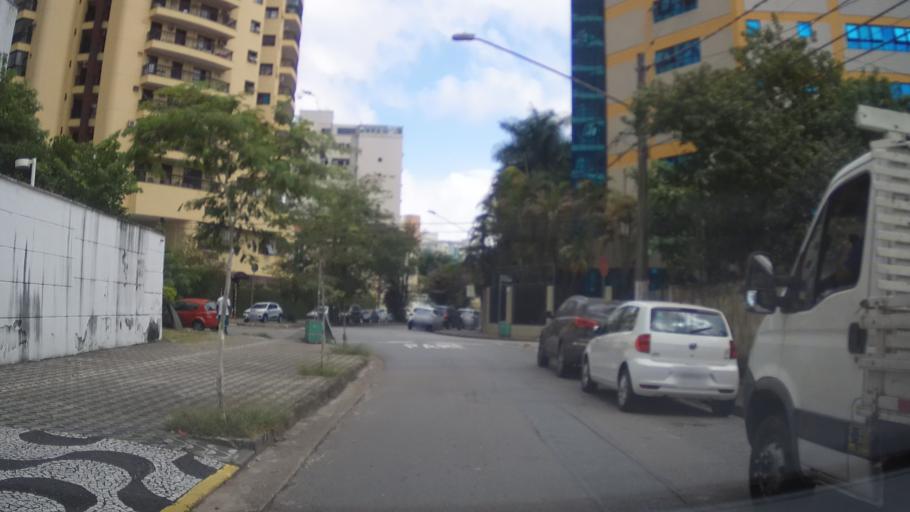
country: BR
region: Sao Paulo
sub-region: Guaruja
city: Guaruja
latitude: -23.9863
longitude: -46.2980
